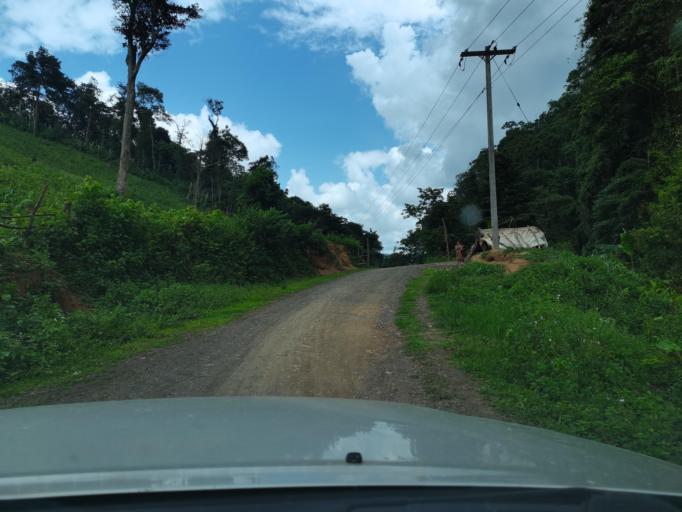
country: LA
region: Loungnamtha
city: Muang Long
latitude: 20.7782
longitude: 101.0167
